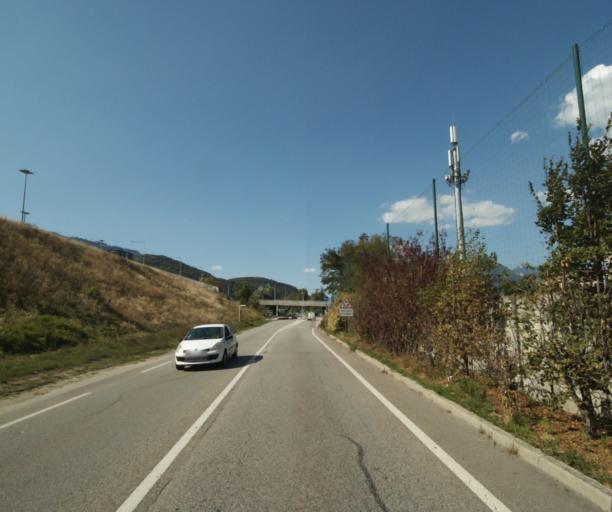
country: FR
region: Rhone-Alpes
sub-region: Departement de l'Isere
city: Seyssinet-Pariset
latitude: 45.1657
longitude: 5.6917
